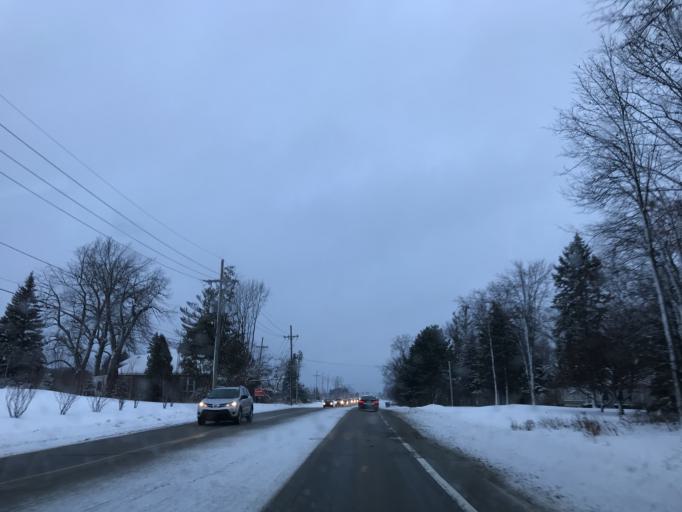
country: US
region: Michigan
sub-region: Oakland County
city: Novi
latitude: 42.4810
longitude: -83.5152
